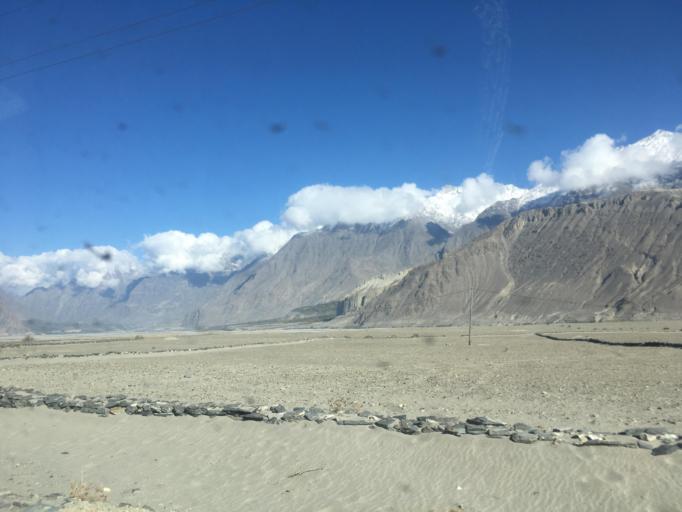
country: PK
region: Gilgit-Baltistan
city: Skardu
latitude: 35.3585
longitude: 75.5368
